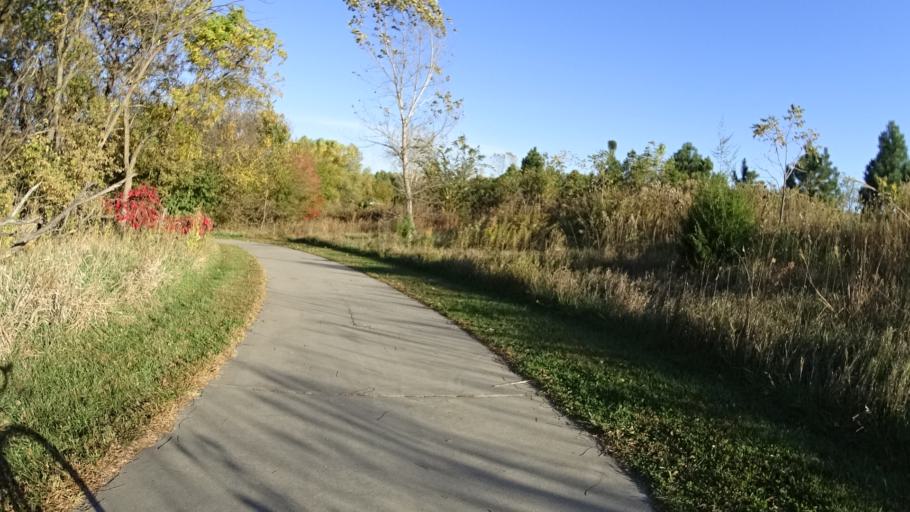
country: US
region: Nebraska
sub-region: Sarpy County
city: Papillion
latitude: 41.1399
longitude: -96.0642
